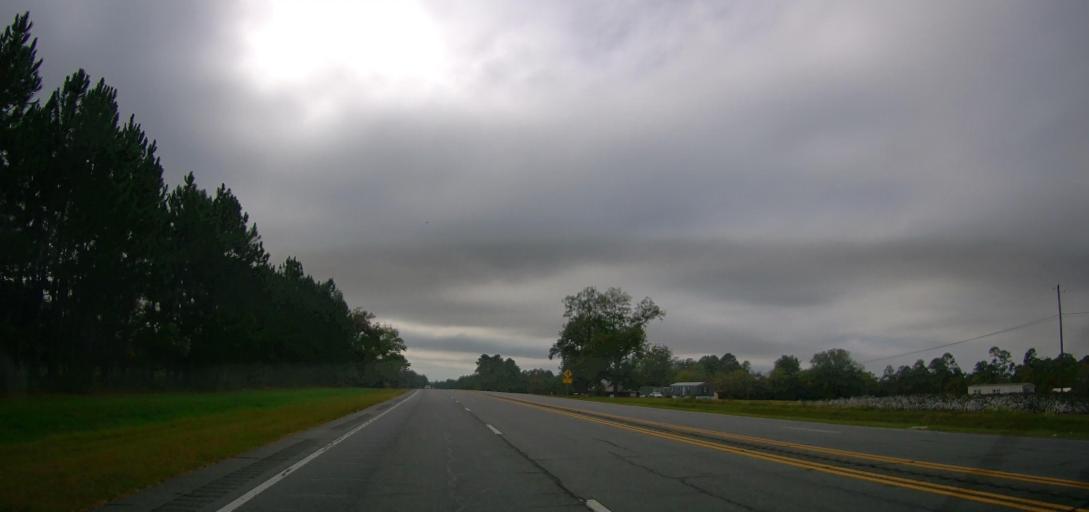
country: US
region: Georgia
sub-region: Colquitt County
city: Moultrie
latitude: 31.2564
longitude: -83.7081
